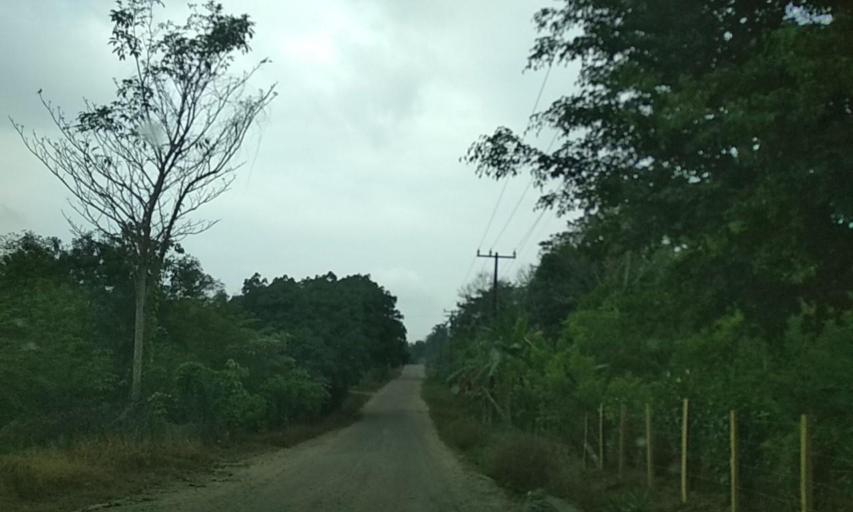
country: MX
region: Veracruz
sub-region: Uxpanapa
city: Poblado 10
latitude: 17.4589
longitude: -94.1032
